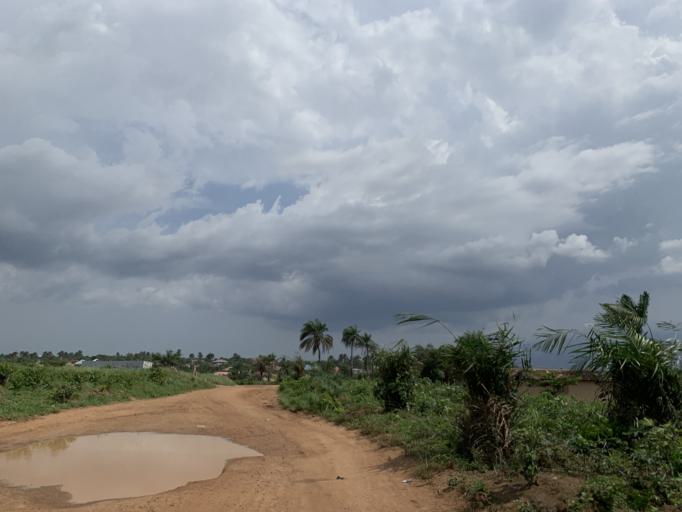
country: SL
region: Western Area
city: Waterloo
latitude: 8.3537
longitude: -13.0492
